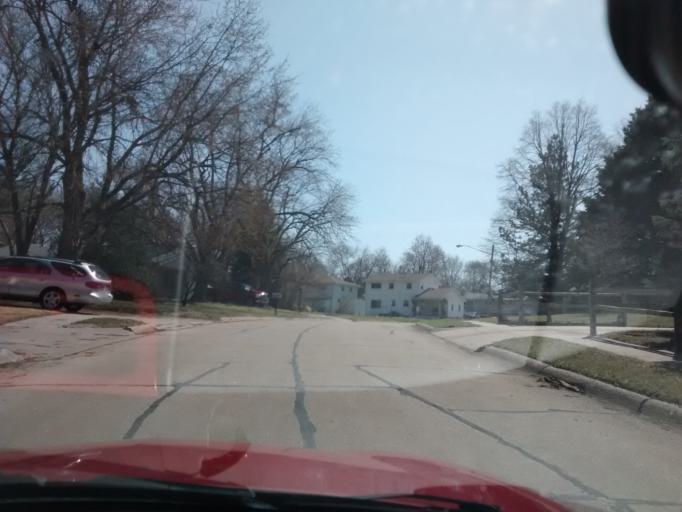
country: US
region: Nebraska
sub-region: Sarpy County
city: Bellevue
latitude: 41.1489
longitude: -95.9123
